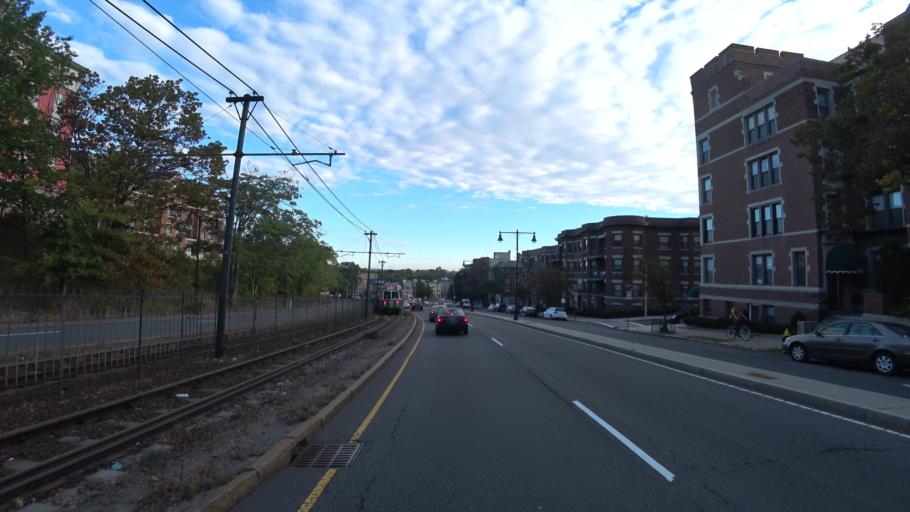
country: US
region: Massachusetts
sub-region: Norfolk County
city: Brookline
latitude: 42.3467
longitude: -71.1409
